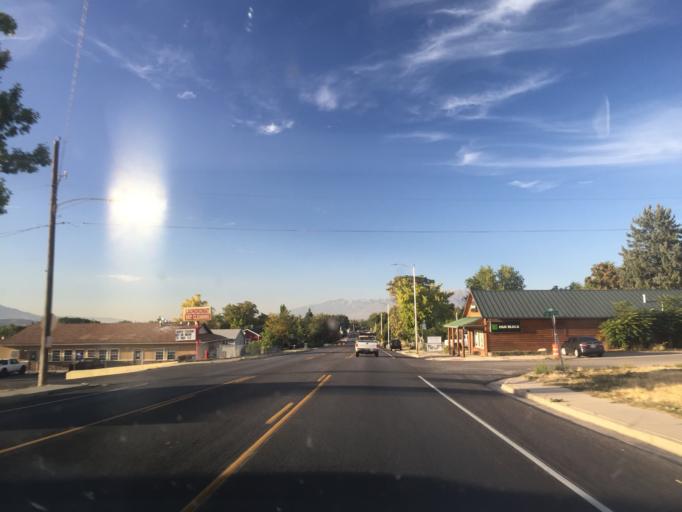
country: US
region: Utah
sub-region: Utah County
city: Payson
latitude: 40.0379
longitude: -111.7338
